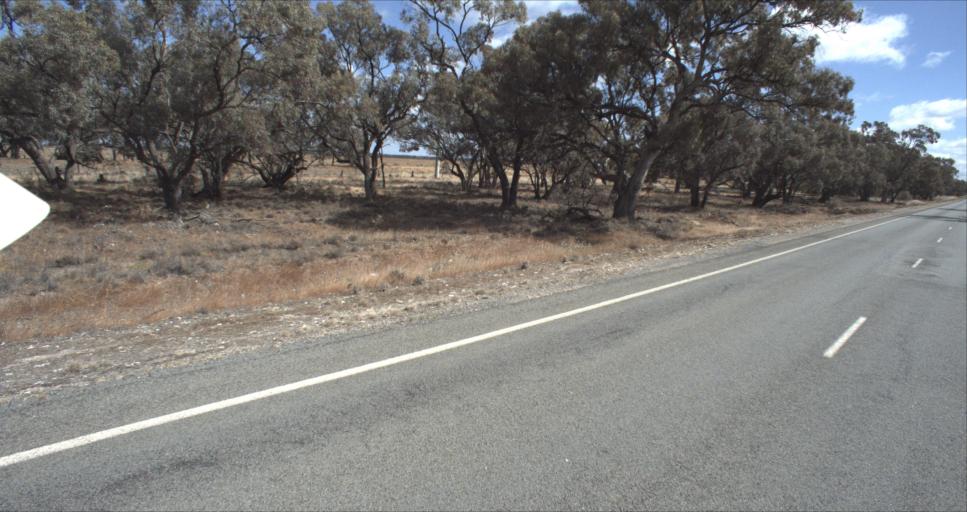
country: AU
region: New South Wales
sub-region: Murrumbidgee Shire
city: Darlington Point
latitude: -34.5654
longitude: 146.1682
